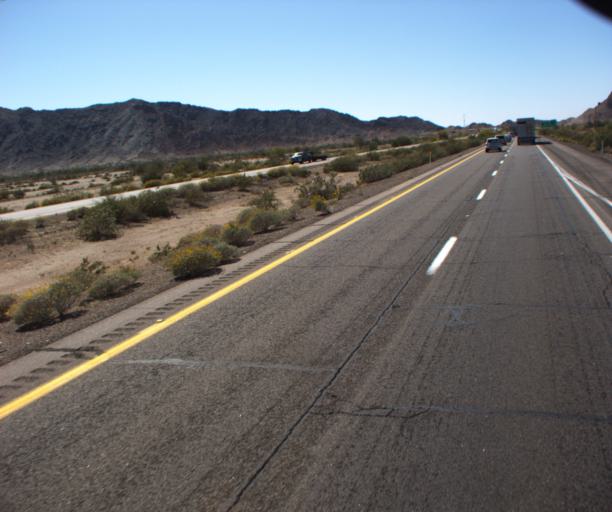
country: US
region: Arizona
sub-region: Yuma County
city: Wellton
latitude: 32.7303
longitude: -113.7227
